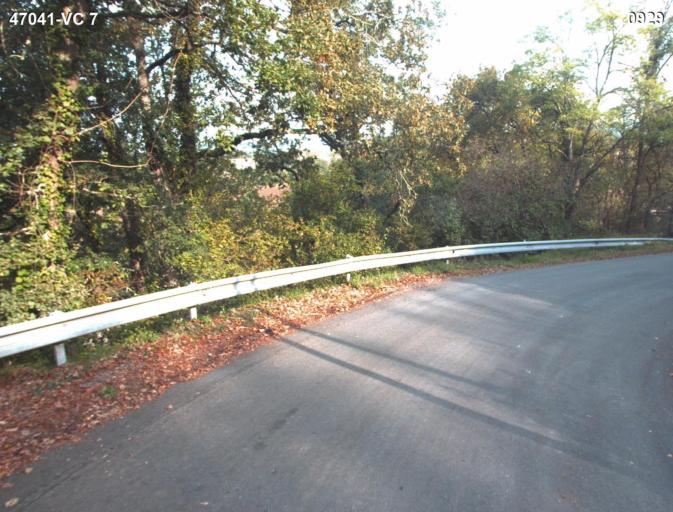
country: FR
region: Aquitaine
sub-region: Departement du Lot-et-Garonne
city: Port-Sainte-Marie
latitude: 44.1981
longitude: 0.4117
